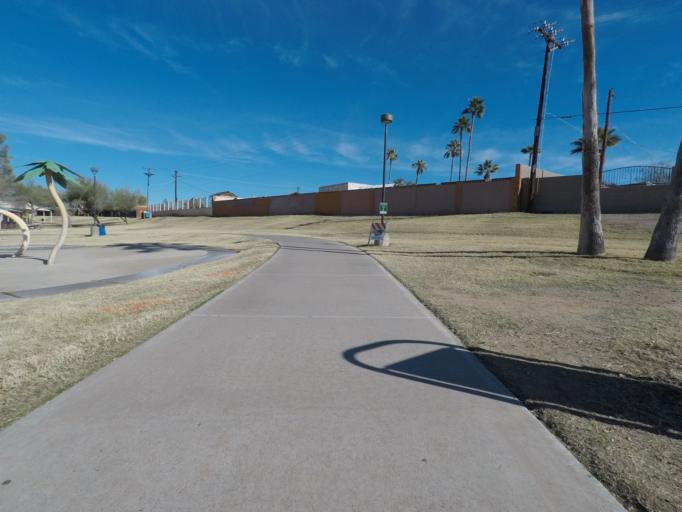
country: US
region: Arizona
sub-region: Maricopa County
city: Tempe
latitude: 33.4602
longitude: -111.9143
